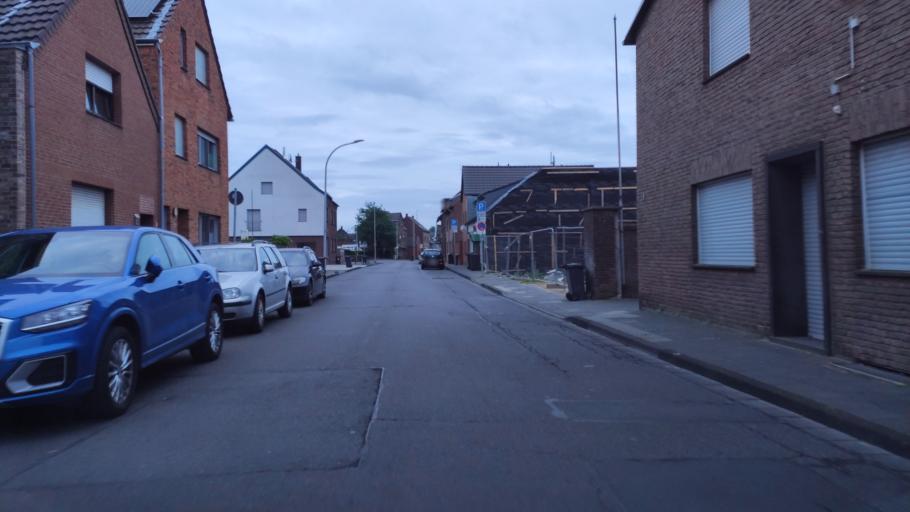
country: DE
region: North Rhine-Westphalia
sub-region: Regierungsbezirk Dusseldorf
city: Dormagen
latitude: 51.1133
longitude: 6.7670
